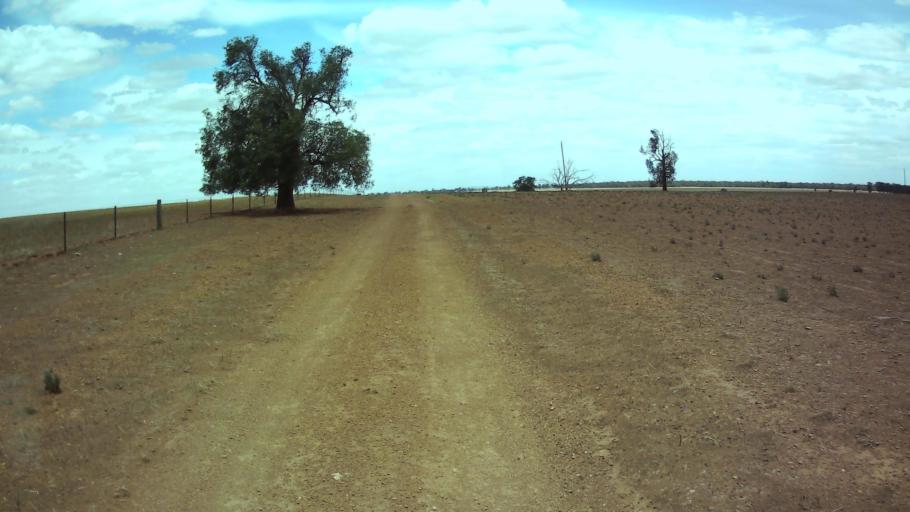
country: AU
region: New South Wales
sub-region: Weddin
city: Grenfell
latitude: -33.9008
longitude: 147.7395
